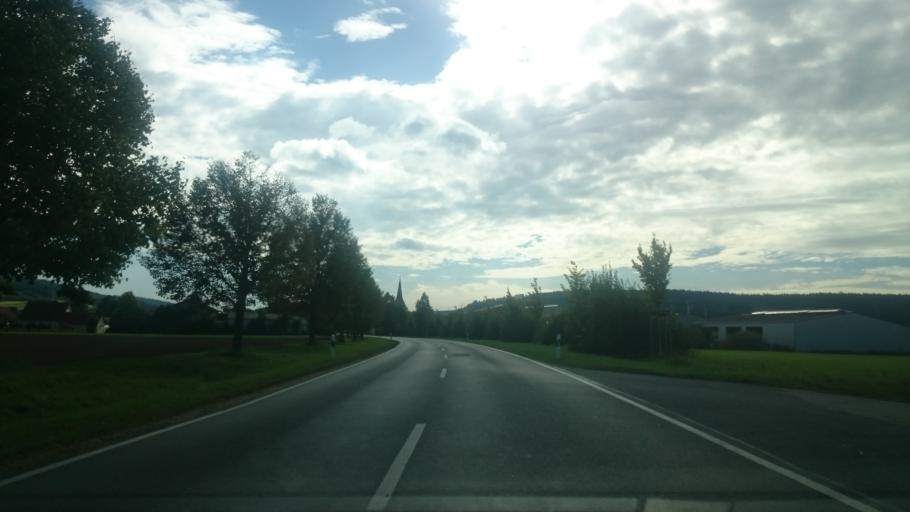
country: DE
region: Bavaria
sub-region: Regierungsbezirk Mittelfranken
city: Thalmassing
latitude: 49.1490
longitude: 11.2591
